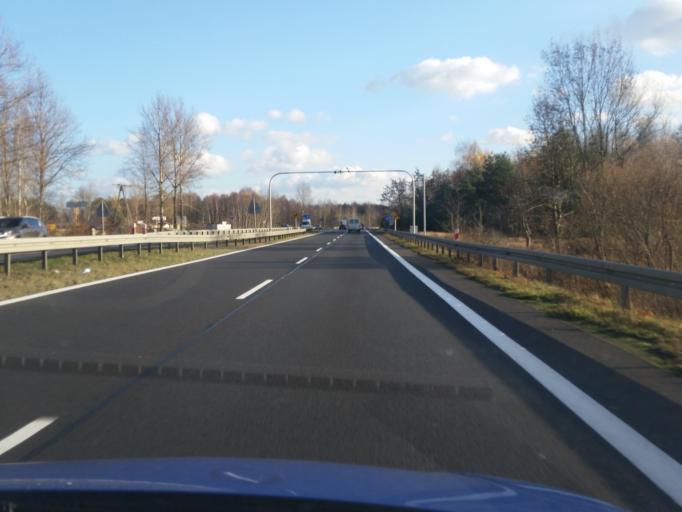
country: PL
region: Silesian Voivodeship
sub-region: Powiat bedzinski
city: Siewierz
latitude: 50.4895
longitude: 19.2123
